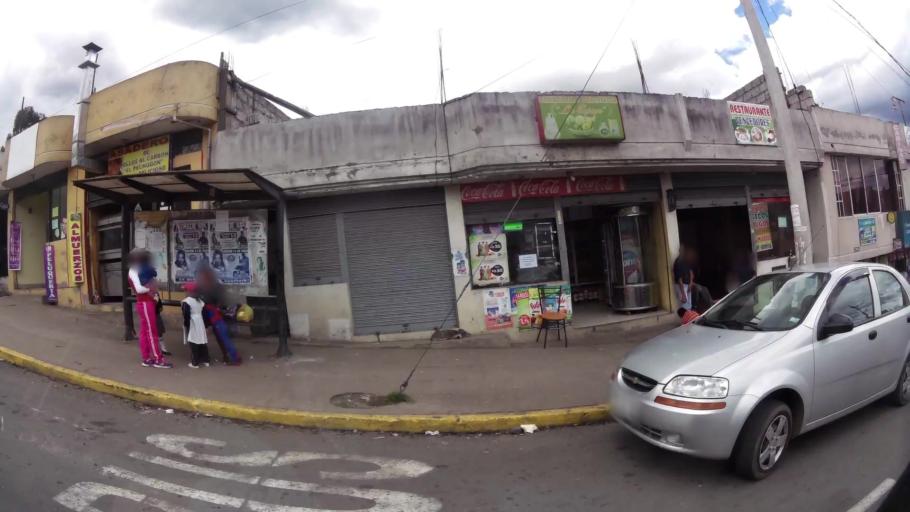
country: EC
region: Pichincha
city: Sangolqui
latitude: -0.3295
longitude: -78.5305
